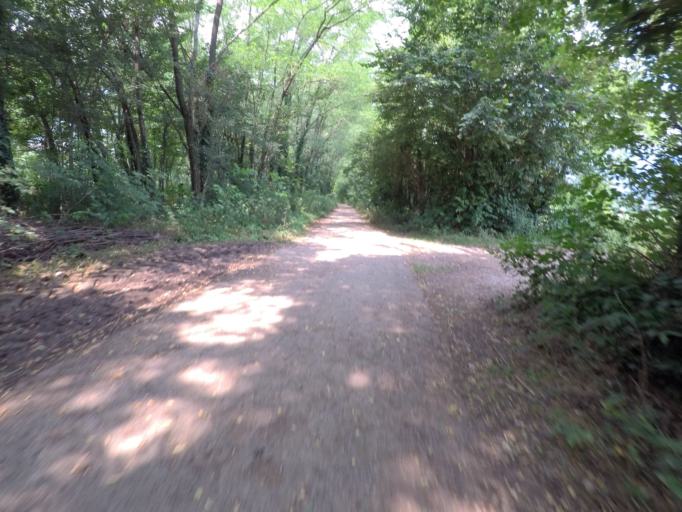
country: IT
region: Friuli Venezia Giulia
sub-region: Provincia di Pordenone
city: Montereale Valcellina
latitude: 46.1332
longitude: 12.6368
